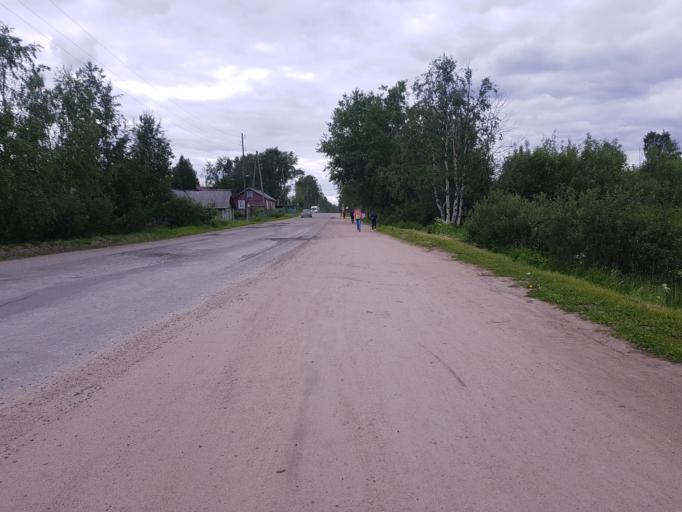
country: RU
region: Republic of Karelia
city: Kalevala
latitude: 65.1999
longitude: 31.1781
